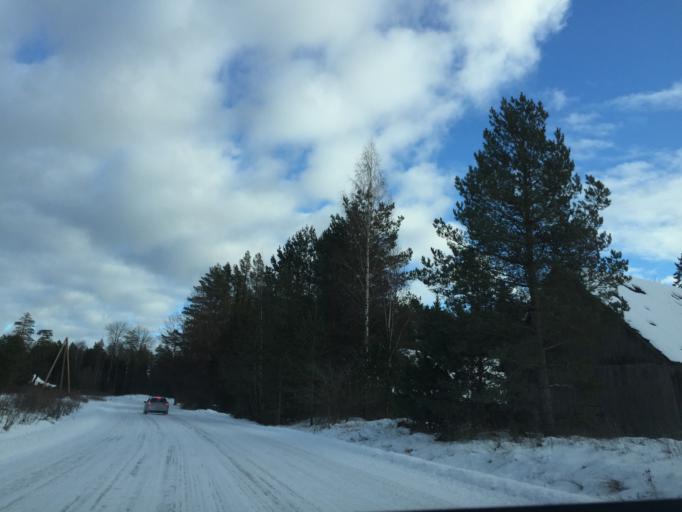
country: LV
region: Ogre
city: Jumprava
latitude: 56.5476
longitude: 24.8659
